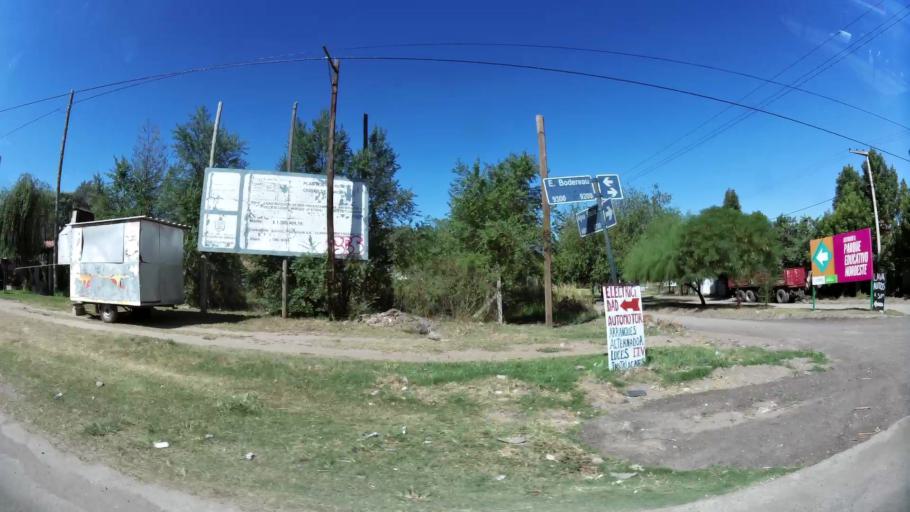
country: AR
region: Cordoba
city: Villa Allende
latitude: -31.3161
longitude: -64.2882
